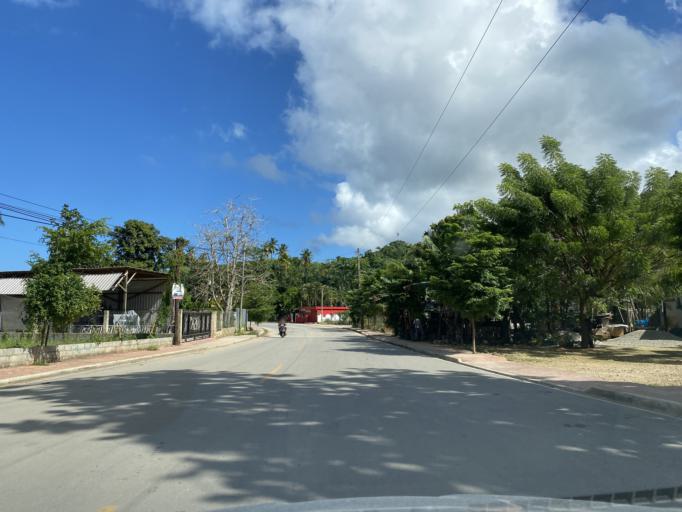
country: DO
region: Samana
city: Las Terrenas
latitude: 19.3023
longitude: -69.5505
